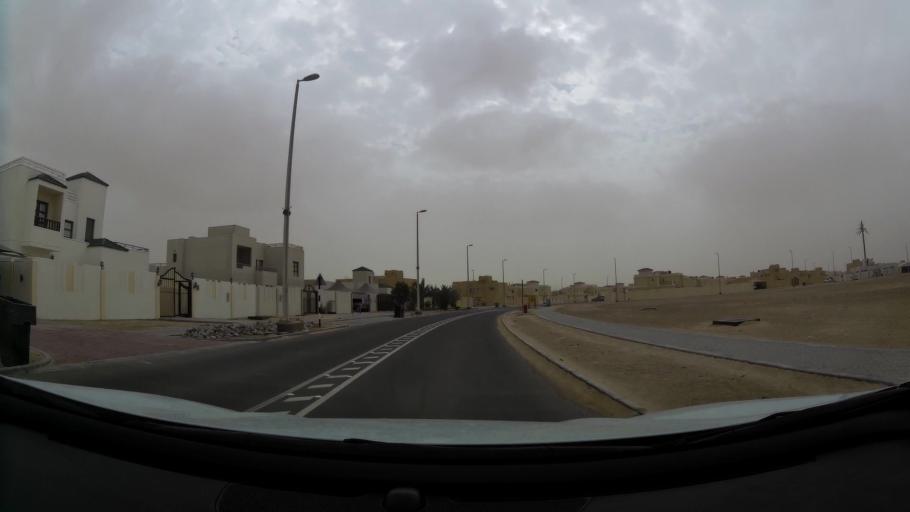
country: AE
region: Abu Dhabi
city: Abu Dhabi
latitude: 24.4538
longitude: 54.7359
